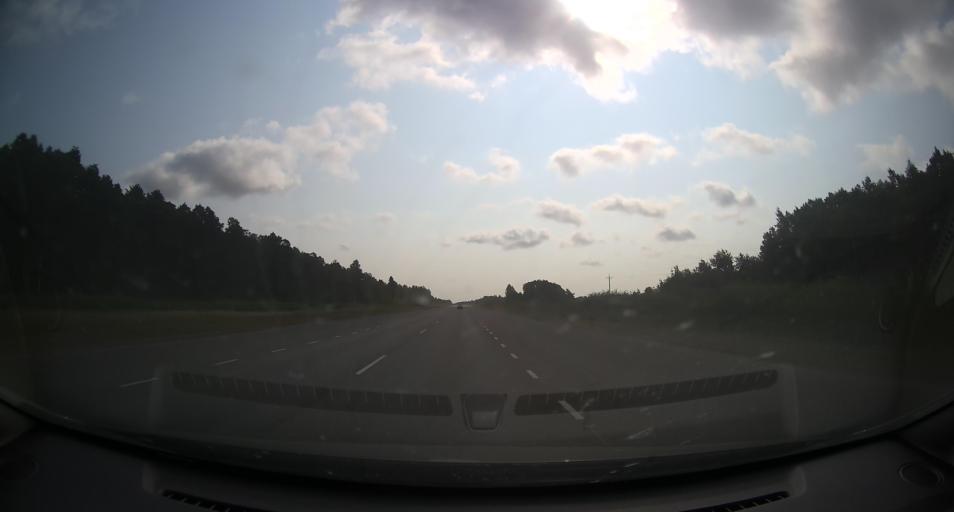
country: EE
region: Laeaene
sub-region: Lihula vald
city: Lihula
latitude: 58.5677
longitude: 23.7847
